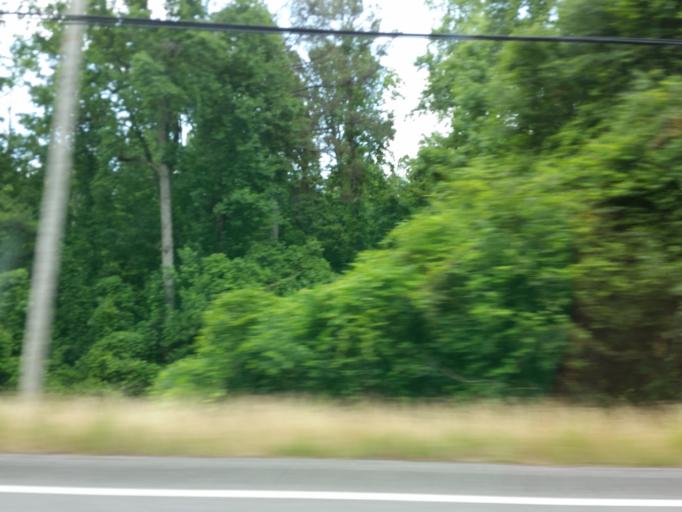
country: US
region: Alabama
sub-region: Sumter County
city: York
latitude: 32.4162
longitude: -88.2398
